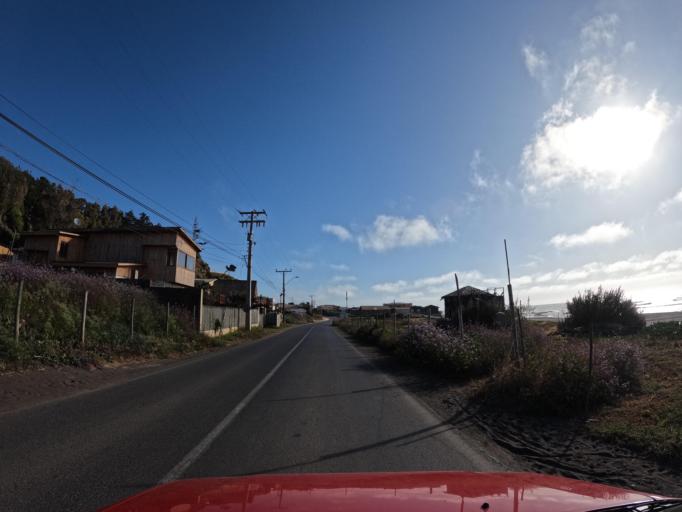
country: CL
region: Maule
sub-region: Provincia de Talca
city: Constitucion
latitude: -34.8933
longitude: -72.1773
